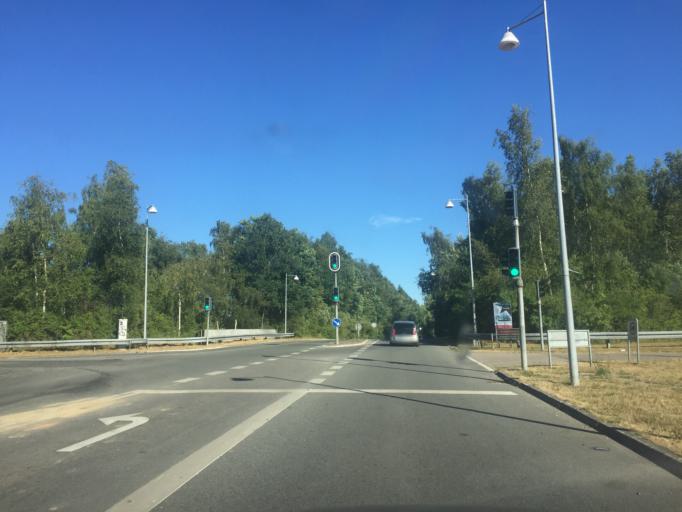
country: DK
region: Capital Region
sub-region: Albertslund Kommune
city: Albertslund
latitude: 55.6724
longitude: 12.3453
